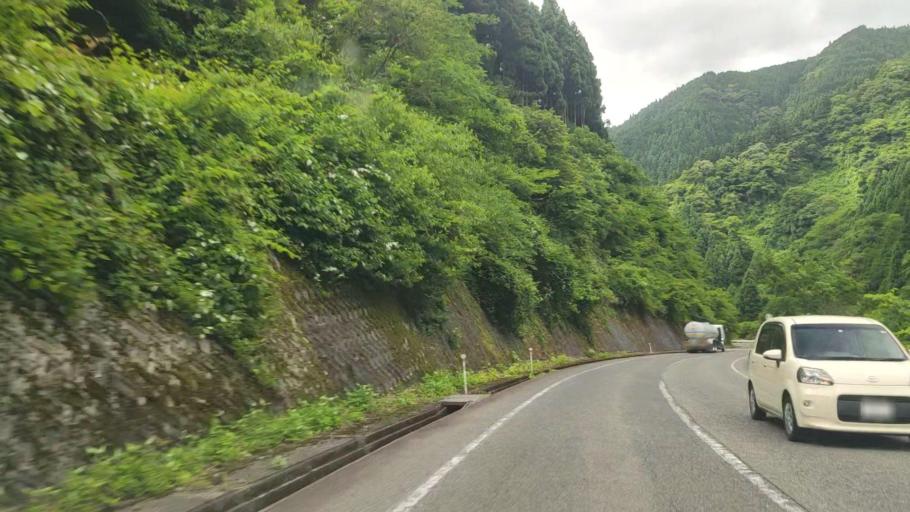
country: JP
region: Tottori
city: Yonago
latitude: 35.2575
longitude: 133.4375
